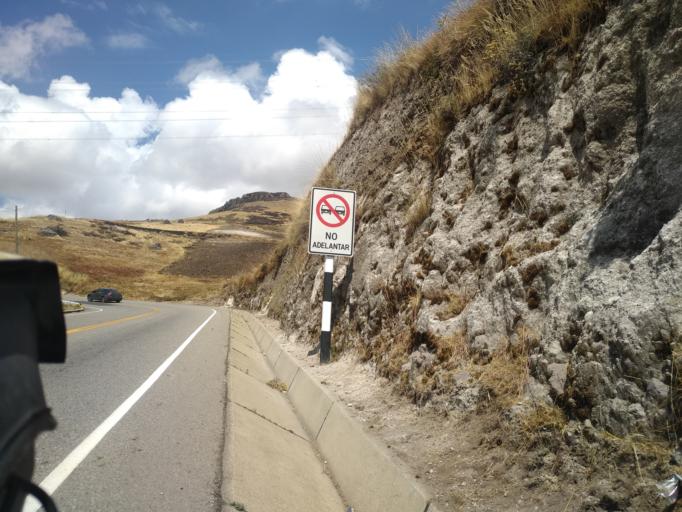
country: PE
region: La Libertad
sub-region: Provincia de Santiago de Chuco
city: Quiruvilca
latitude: -7.9216
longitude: -78.1526
